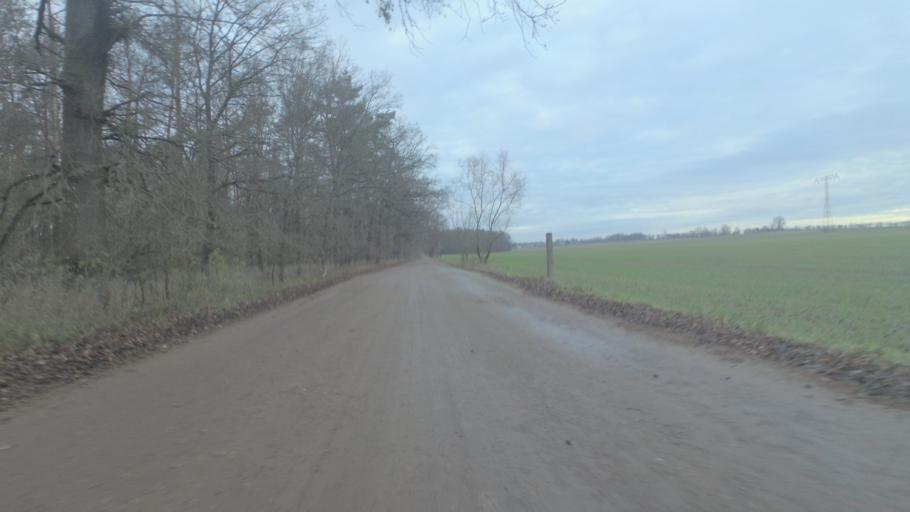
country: DE
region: Brandenburg
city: Am Mellensee
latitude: 52.2362
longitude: 13.3461
